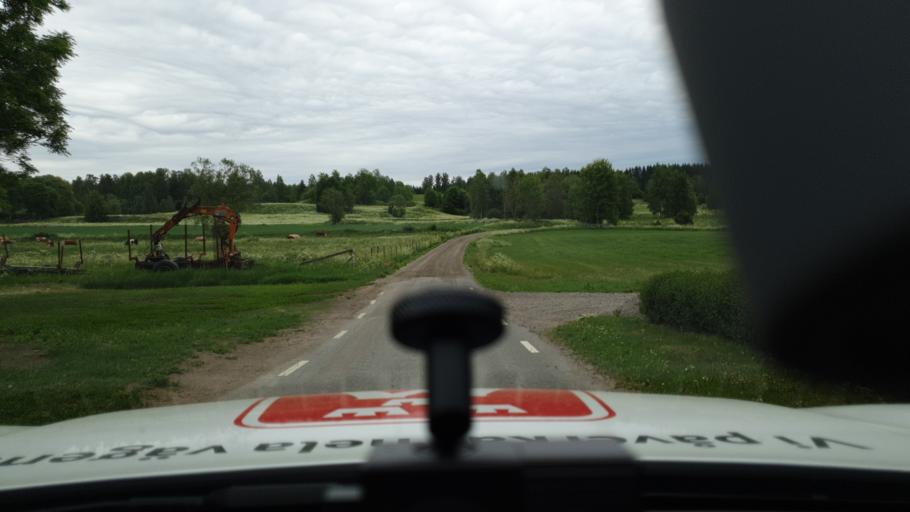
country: SE
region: Vaestra Goetaland
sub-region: Falkopings Kommun
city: Falkoeping
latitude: 58.0631
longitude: 13.6635
